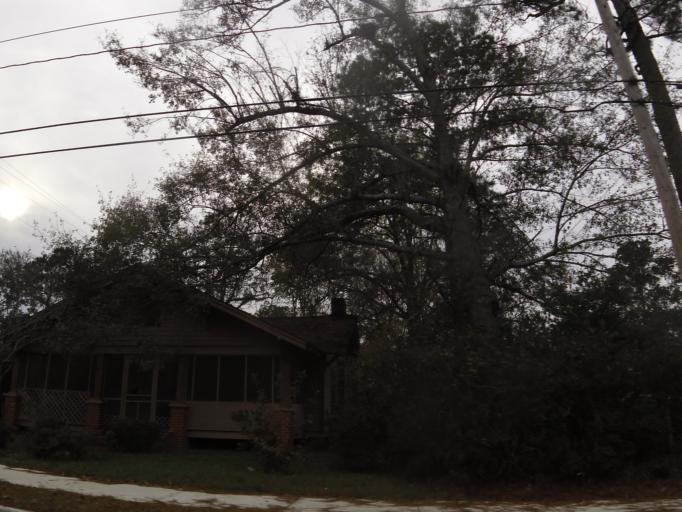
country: US
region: Georgia
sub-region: Thomas County
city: Thomasville
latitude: 30.8187
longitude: -83.9794
